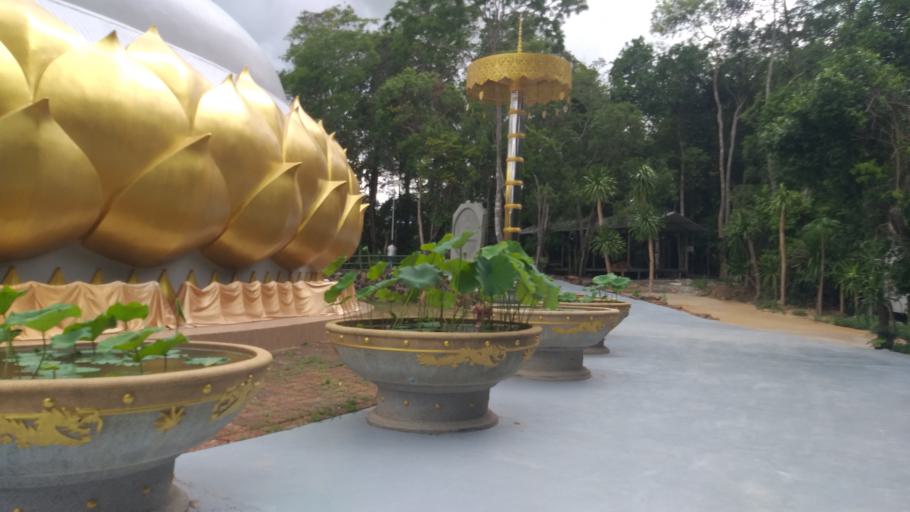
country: TH
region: Nakhon Ratchasima
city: Sikhio
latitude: 14.6847
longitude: 101.6917
